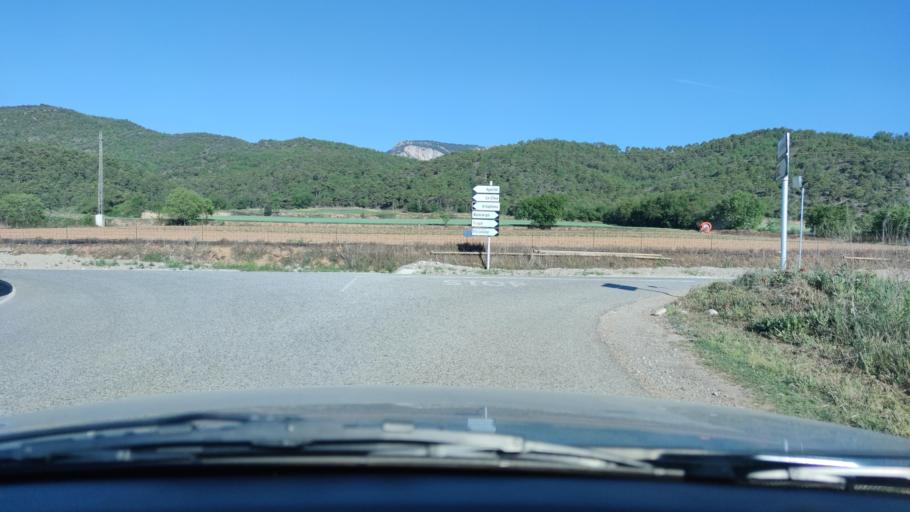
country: ES
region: Catalonia
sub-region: Provincia de Lleida
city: Oliana
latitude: 42.0354
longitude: 1.2878
